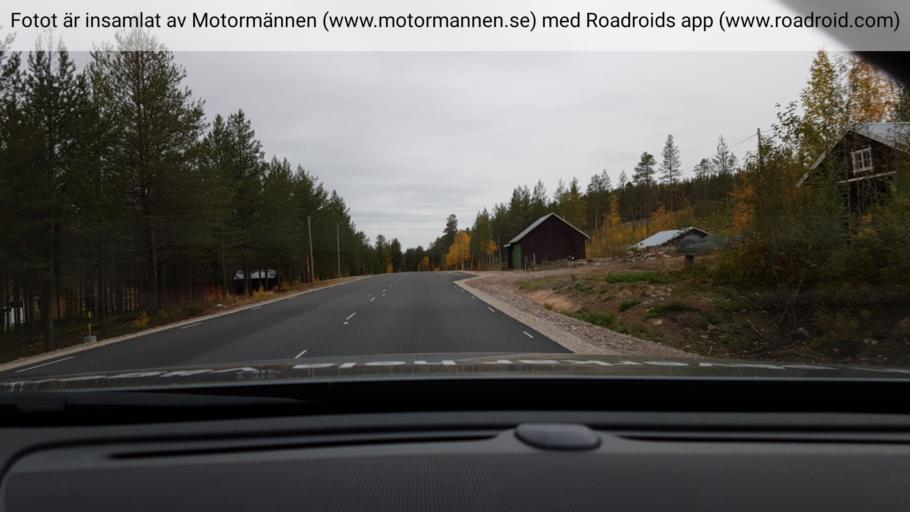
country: SE
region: Norrbotten
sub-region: Overkalix Kommun
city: OEverkalix
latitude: 66.3909
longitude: 22.8204
